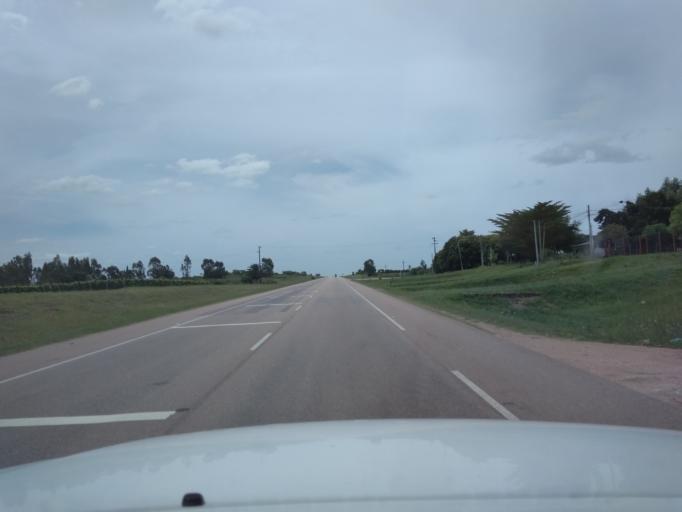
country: UY
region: Canelones
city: Canelones
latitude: -34.4939
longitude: -56.2819
